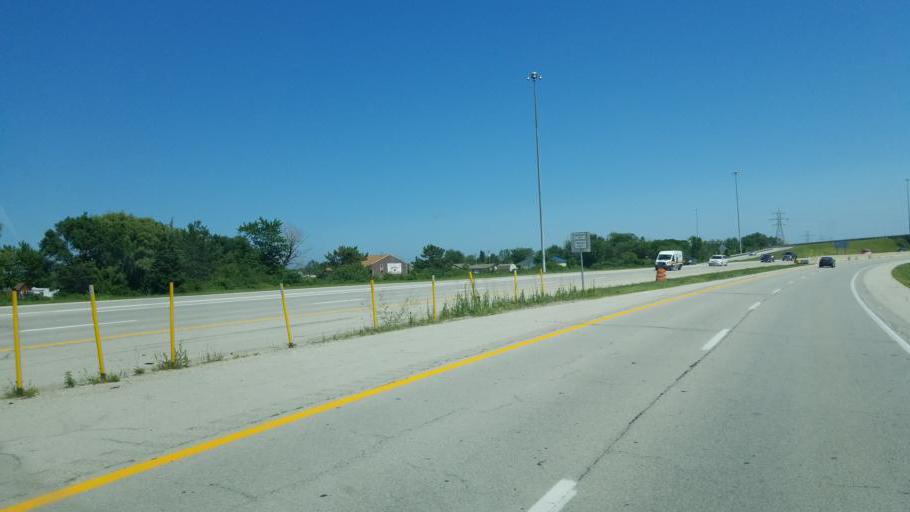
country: US
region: Ohio
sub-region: Ottawa County
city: Port Clinton
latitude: 41.5051
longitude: -82.8428
